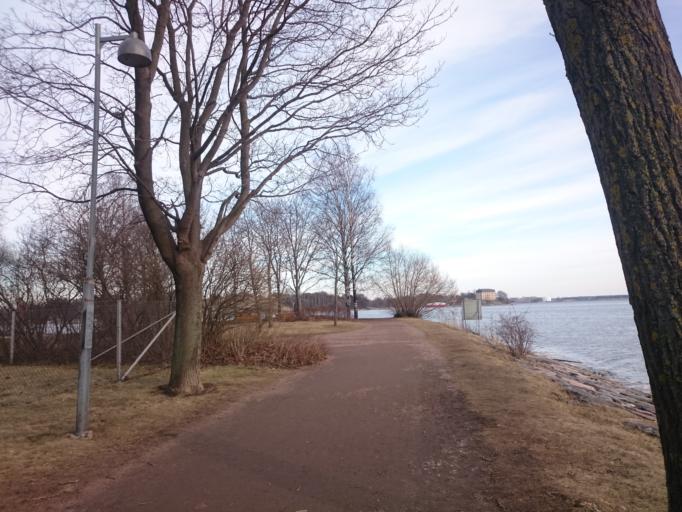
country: FI
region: Uusimaa
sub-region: Helsinki
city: Helsinki
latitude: 60.1728
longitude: 24.9690
